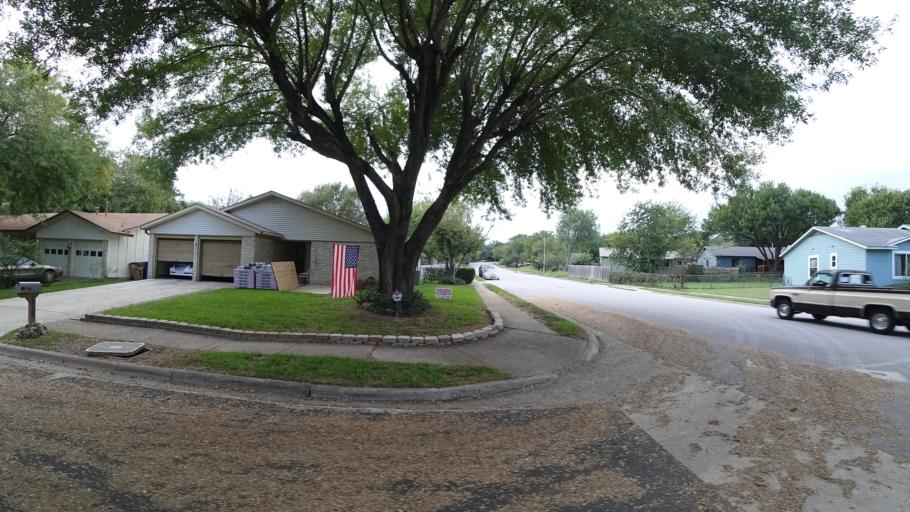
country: US
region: Texas
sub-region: Travis County
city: Onion Creek
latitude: 30.1919
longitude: -97.7924
